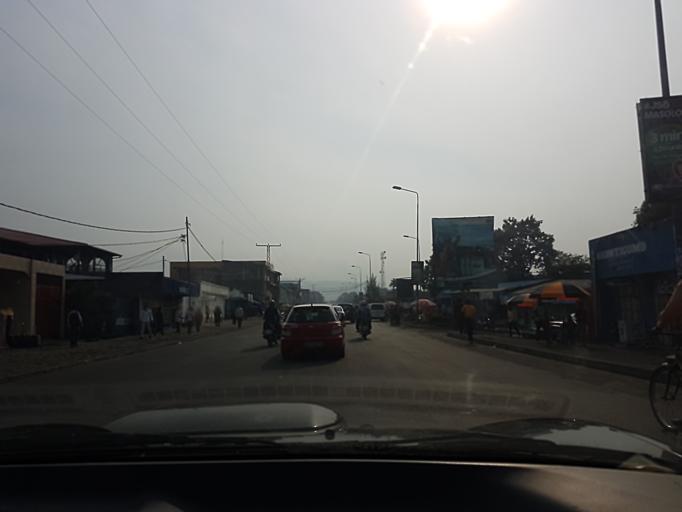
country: CD
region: Nord Kivu
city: Goma
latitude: -1.6782
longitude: 29.2231
